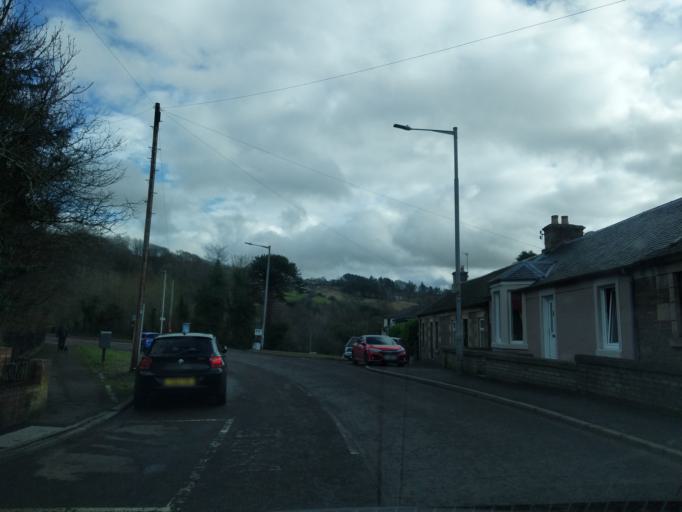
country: GB
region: Scotland
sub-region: South Lanarkshire
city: Lanark
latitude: 55.6753
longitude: -3.8031
